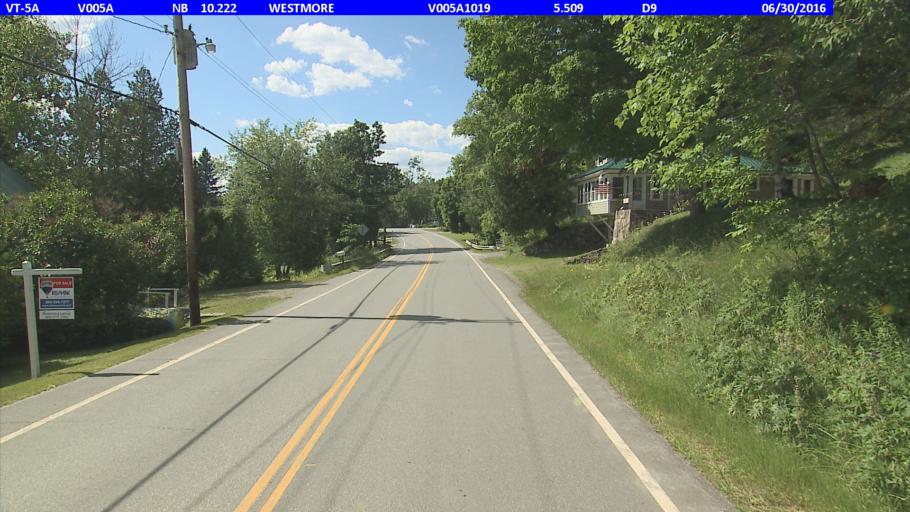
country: US
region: Vermont
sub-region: Orleans County
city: Newport
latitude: 44.7698
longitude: -72.0537
